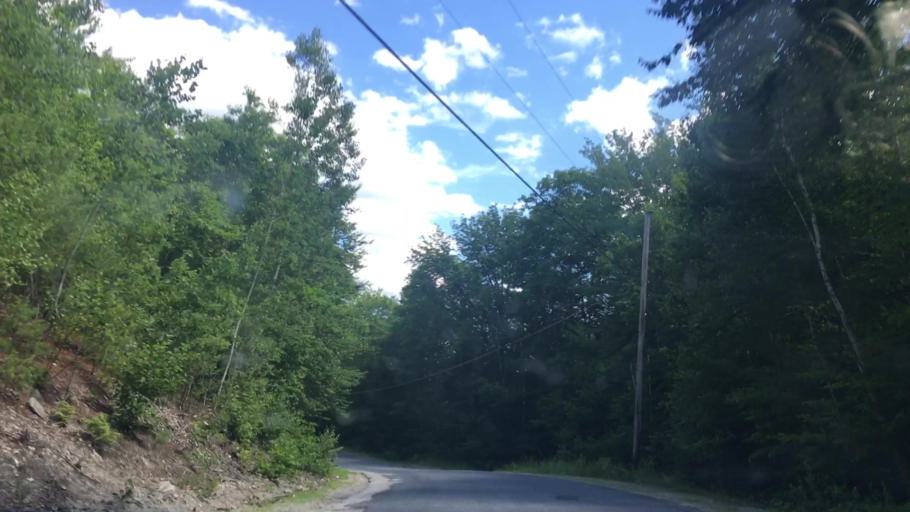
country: US
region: Maine
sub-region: Franklin County
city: Chesterville
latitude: 44.5598
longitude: -70.1283
